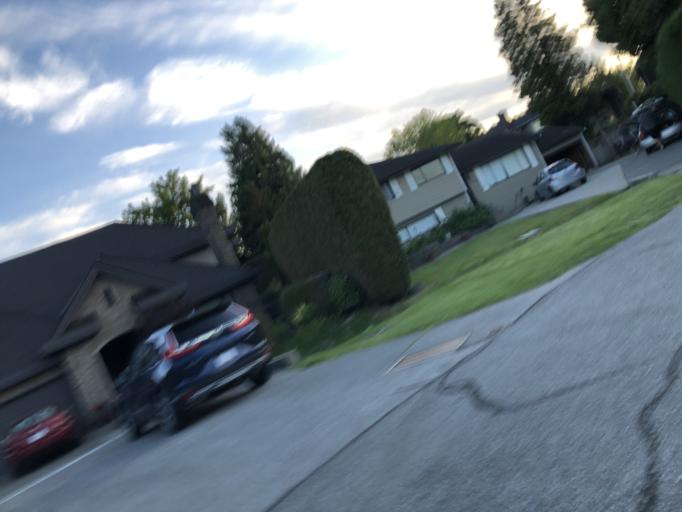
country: CA
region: British Columbia
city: Richmond
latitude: 49.1427
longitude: -123.1225
